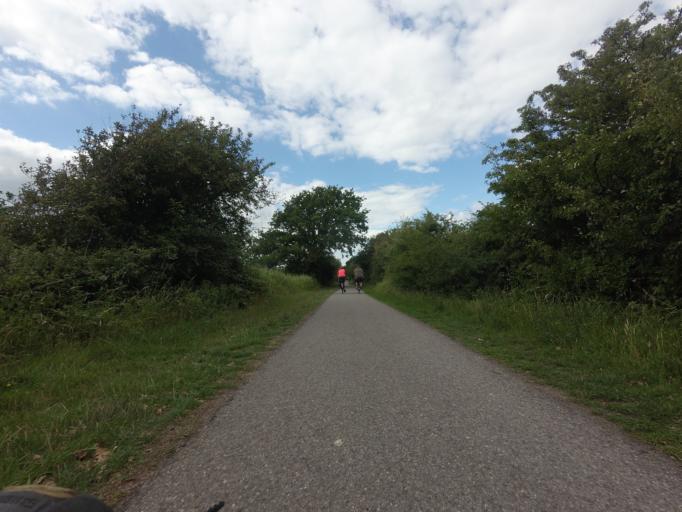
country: GB
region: England
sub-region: East Sussex
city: Hailsham
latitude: 50.8346
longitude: 0.2503
